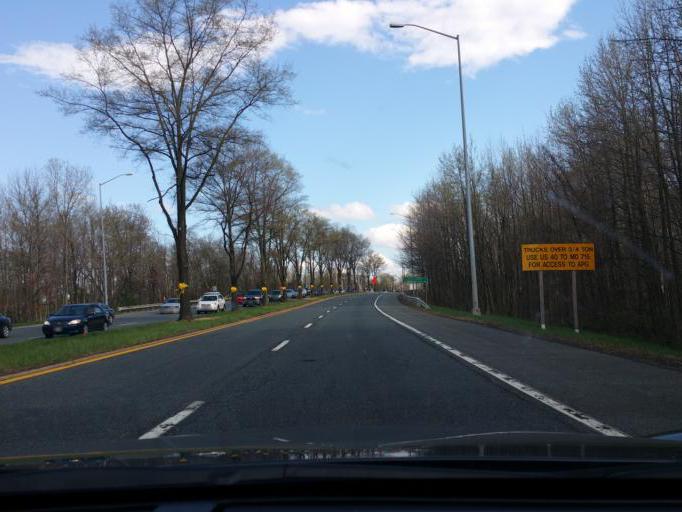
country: US
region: Maryland
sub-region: Harford County
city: Aberdeen
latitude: 39.5178
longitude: -76.1612
